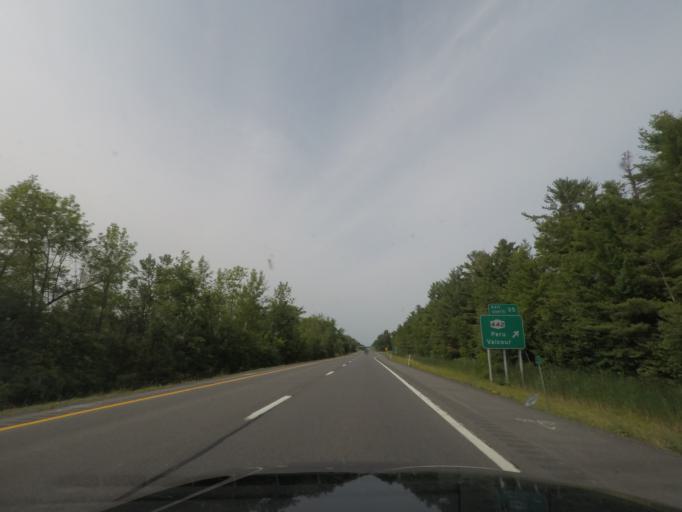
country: US
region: New York
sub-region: Clinton County
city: Peru
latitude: 44.5724
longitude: -73.5028
